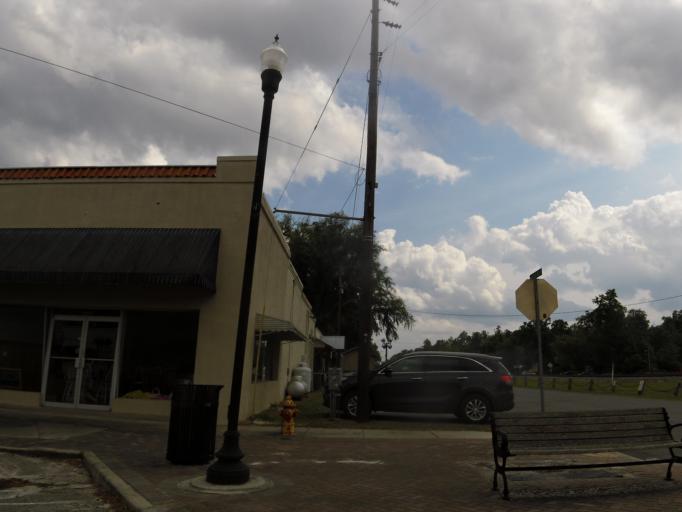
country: US
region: Georgia
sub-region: Charlton County
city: Folkston
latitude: 30.8312
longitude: -82.0077
